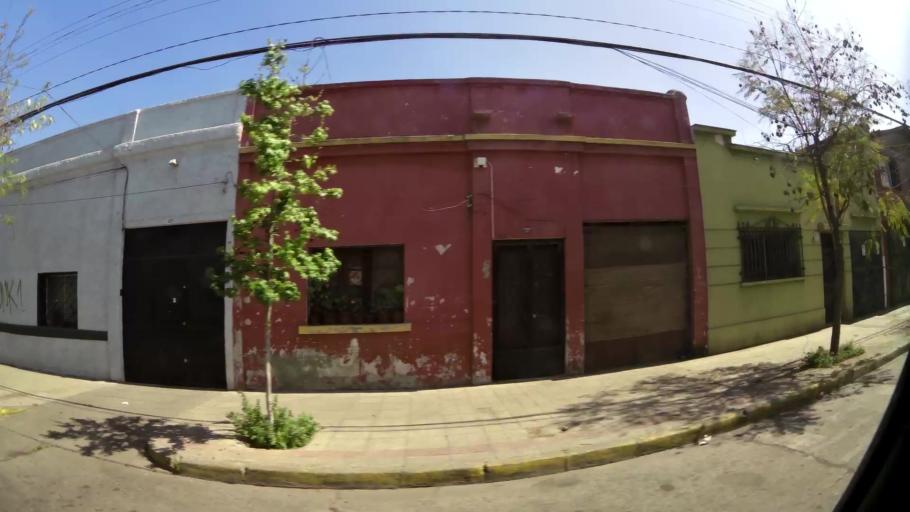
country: CL
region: Santiago Metropolitan
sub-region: Provincia de Santiago
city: Santiago
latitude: -33.4600
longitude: -70.6337
